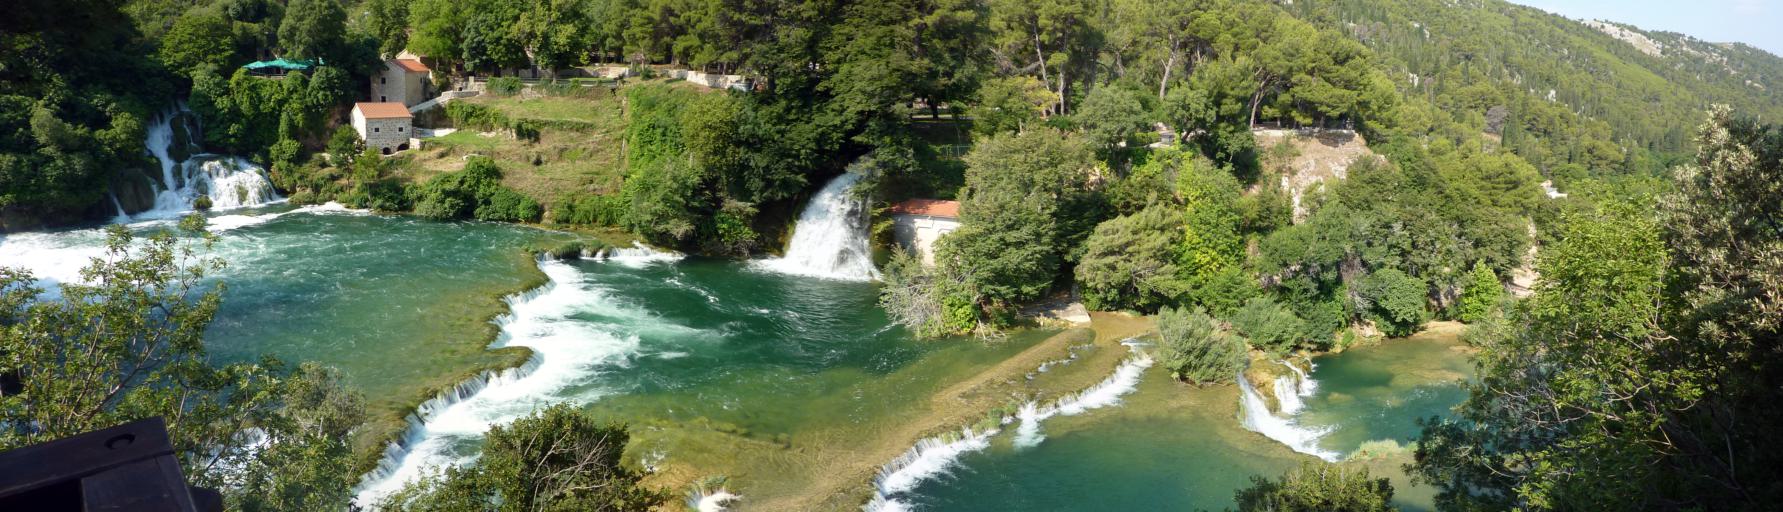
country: HR
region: Sibensko-Kniniska
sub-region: Grad Sibenik
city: Sibenik
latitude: 43.8037
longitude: 15.9652
